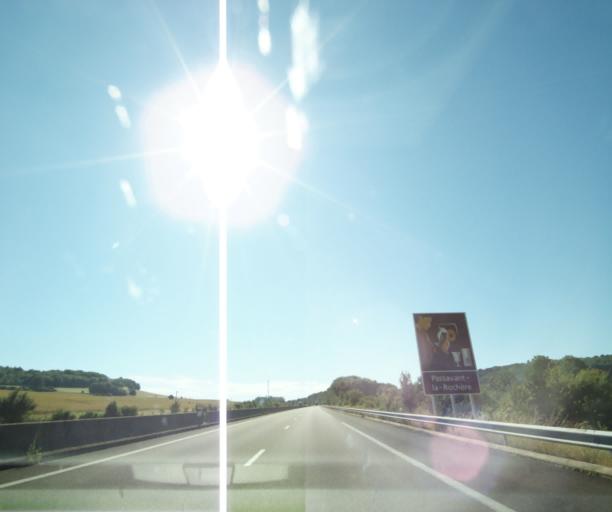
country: FR
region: Champagne-Ardenne
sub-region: Departement de la Haute-Marne
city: Nogent-le-Bas
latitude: 47.9553
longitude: 5.4167
